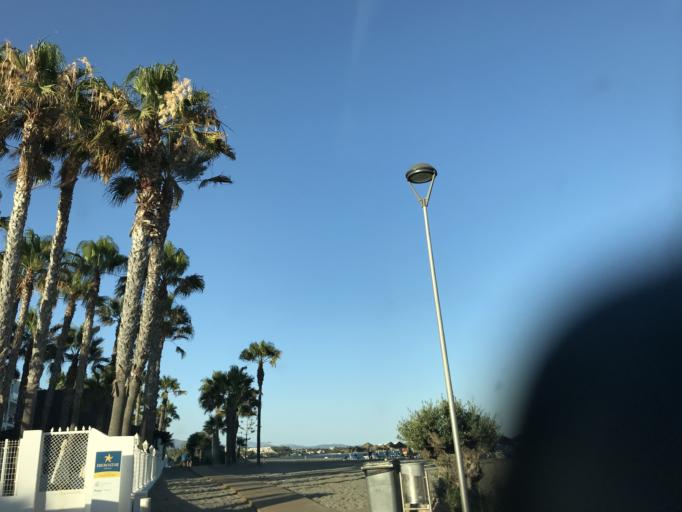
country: ES
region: Andalusia
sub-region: Provincia de Malaga
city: Benahavis
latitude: 36.4558
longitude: -5.0475
